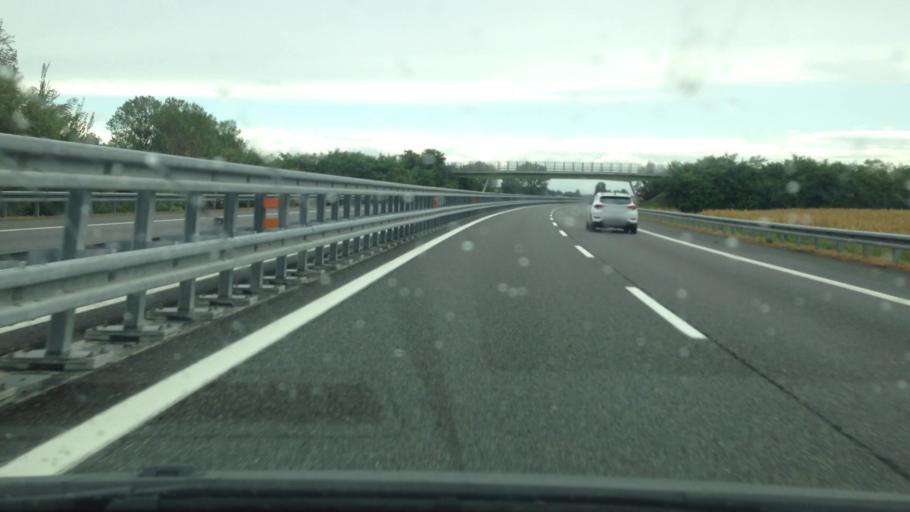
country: IT
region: Piedmont
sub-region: Provincia di Alessandria
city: Valle San Bartolomeo
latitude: 44.9416
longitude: 8.6497
